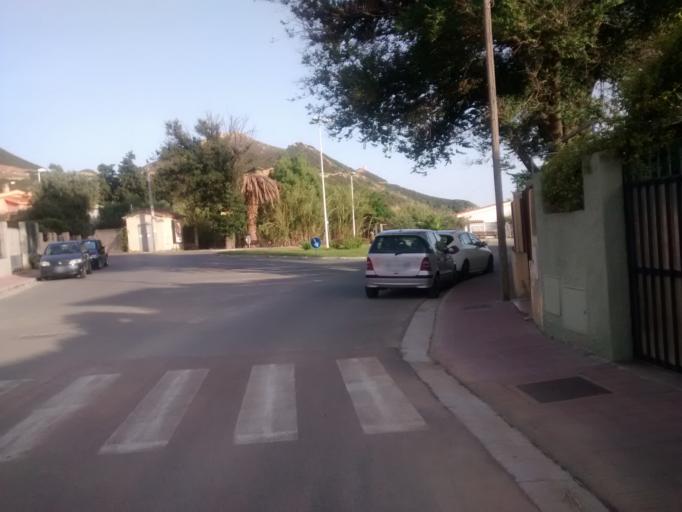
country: IT
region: Sardinia
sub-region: Provincia di Cagliari
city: Villasimius
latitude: 39.1362
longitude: 9.4314
